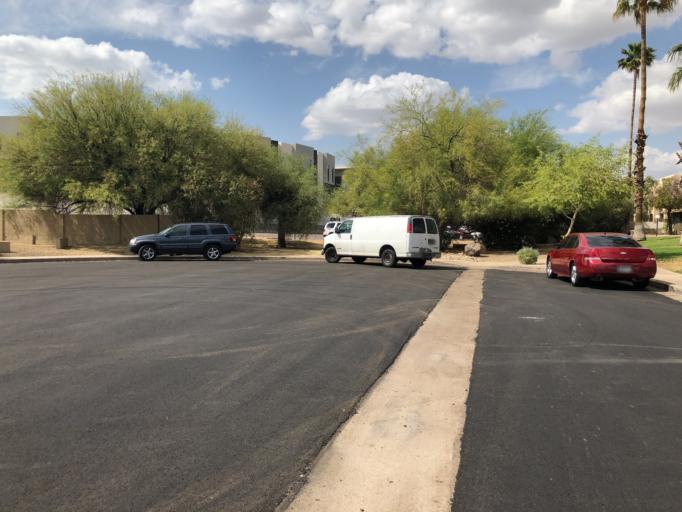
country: US
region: Arizona
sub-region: Maricopa County
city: Scottsdale
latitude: 33.4626
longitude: -111.8994
